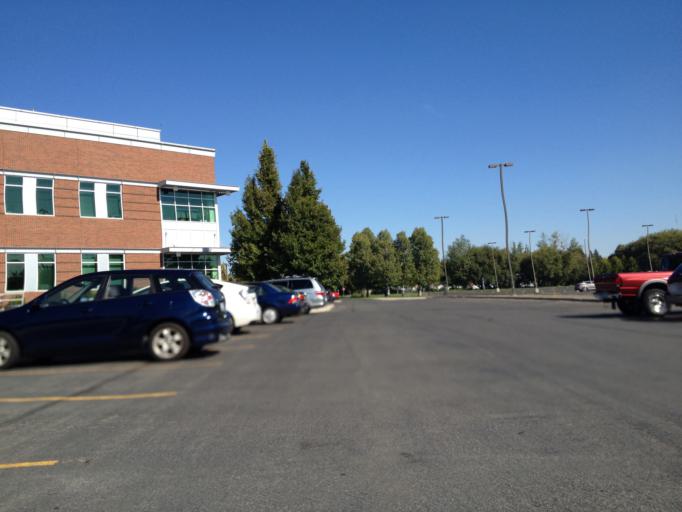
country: US
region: Washington
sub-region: Kittitas County
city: Ellensburg
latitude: 47.0051
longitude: -120.5348
